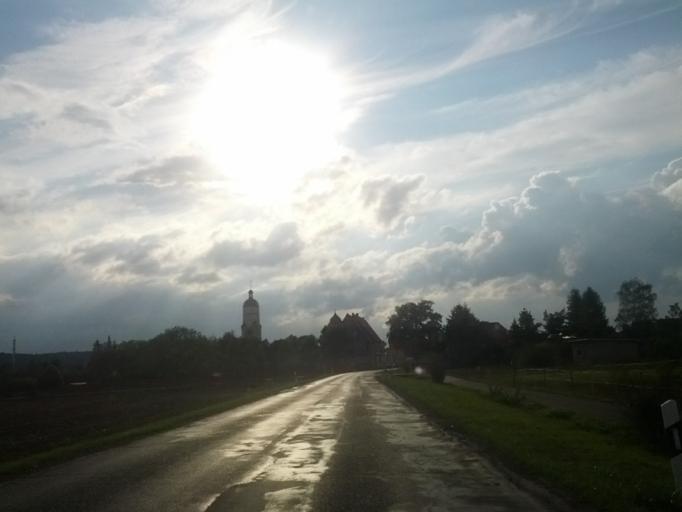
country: DE
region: Thuringia
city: Wandersleben
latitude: 50.8980
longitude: 10.8577
